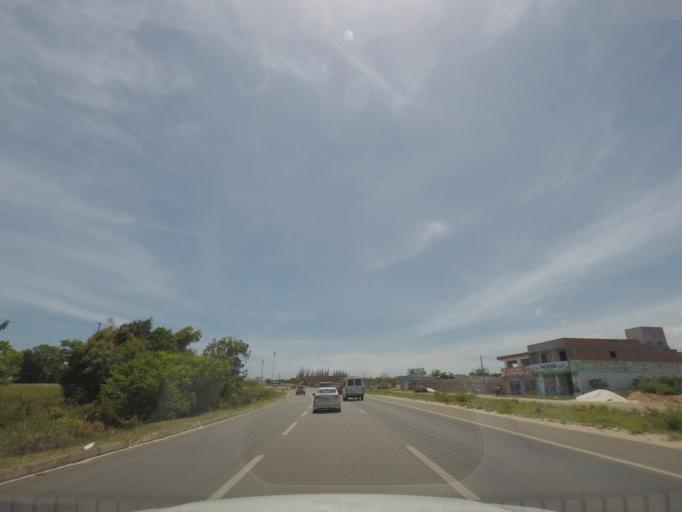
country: BR
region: Bahia
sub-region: Mata De Sao Joao
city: Mata de Sao Joao
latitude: -12.5990
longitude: -38.0454
